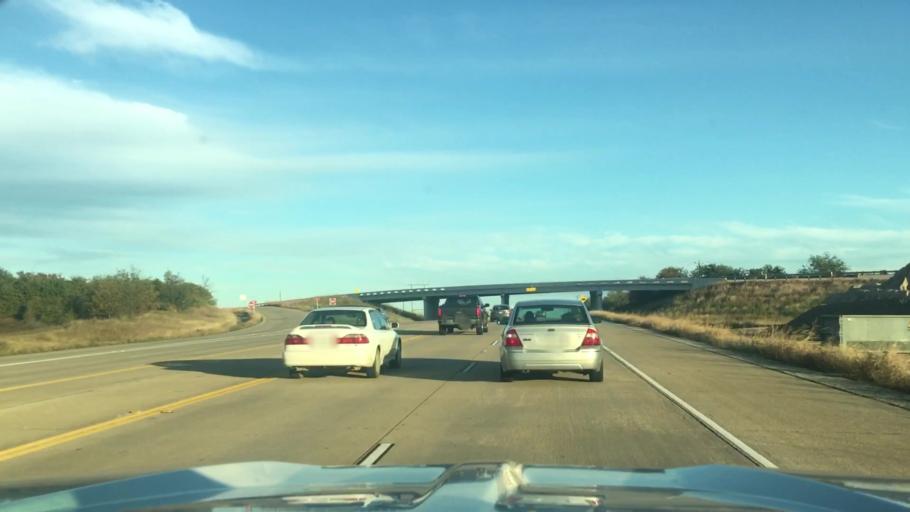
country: US
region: Texas
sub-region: Denton County
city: Cross Roads
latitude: 33.2326
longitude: -97.0062
